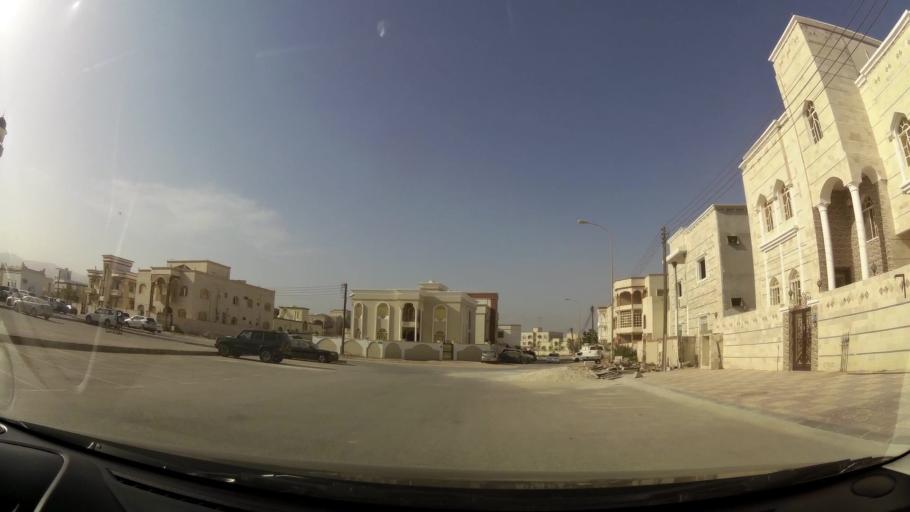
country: OM
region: Zufar
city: Salalah
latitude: 17.0137
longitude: 54.0186
